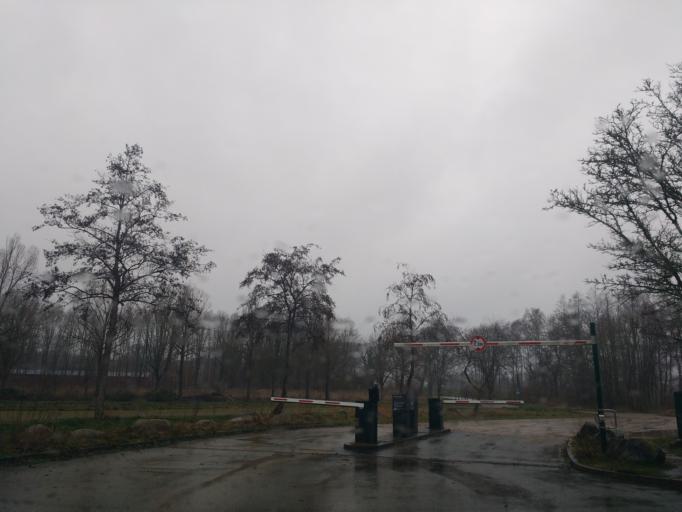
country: DE
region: Schleswig-Holstein
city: Wangels
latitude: 54.3042
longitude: 10.7731
